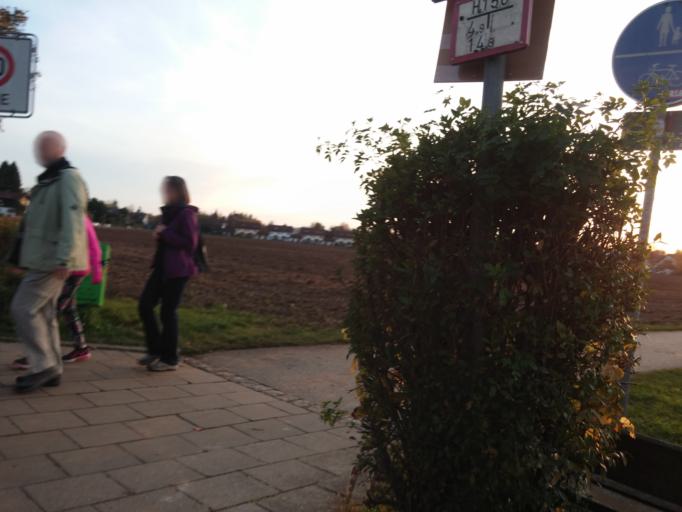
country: DE
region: Bavaria
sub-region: Upper Bavaria
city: Vaterstetten
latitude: 48.1060
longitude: 11.7741
